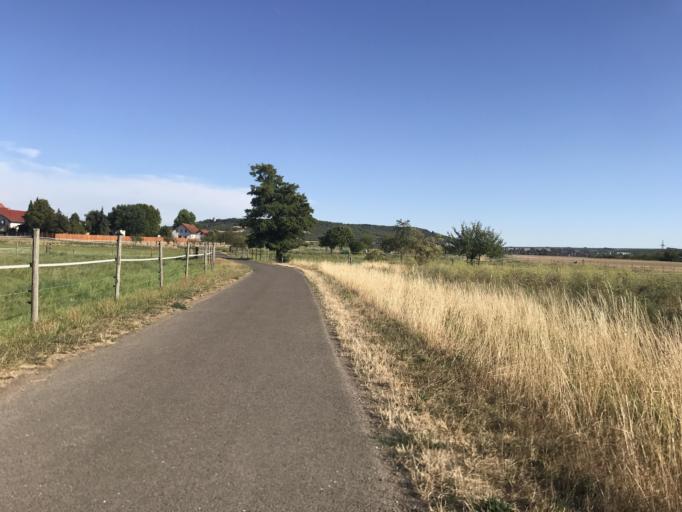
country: DE
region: Rheinland-Pfalz
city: Oestrich-Winkel
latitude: 49.9769
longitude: 8.0042
